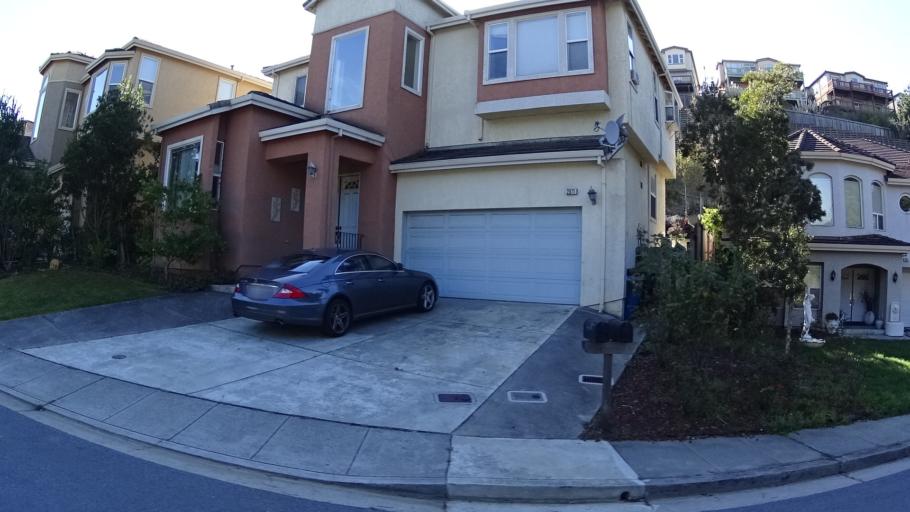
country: US
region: California
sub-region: San Mateo County
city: Pacifica
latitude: 37.6312
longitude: -122.4545
